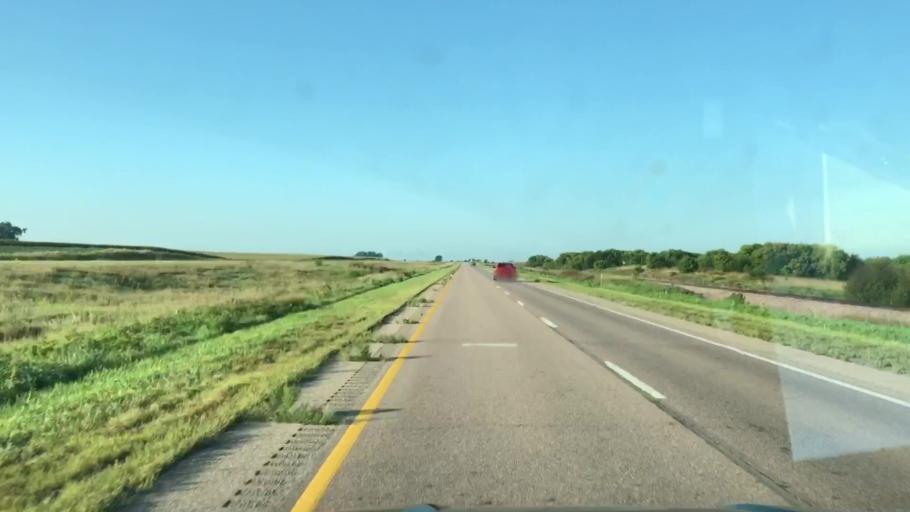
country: US
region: Iowa
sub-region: O'Brien County
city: Sheldon
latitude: 43.1185
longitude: -95.8918
